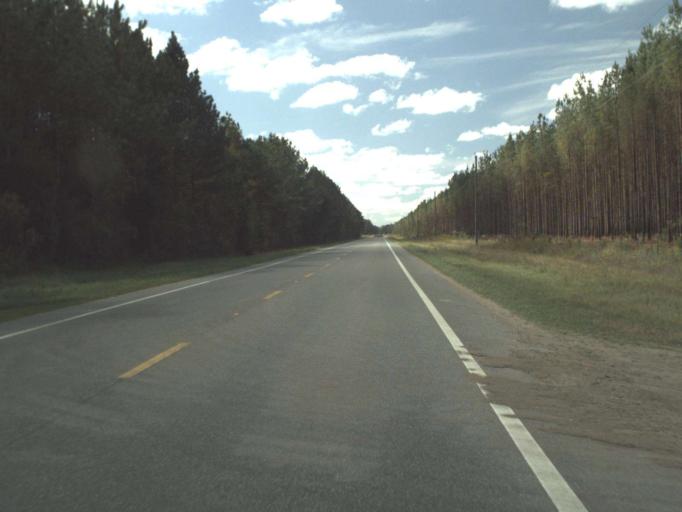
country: US
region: Florida
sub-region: Holmes County
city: Bonifay
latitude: 30.6584
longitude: -85.6582
